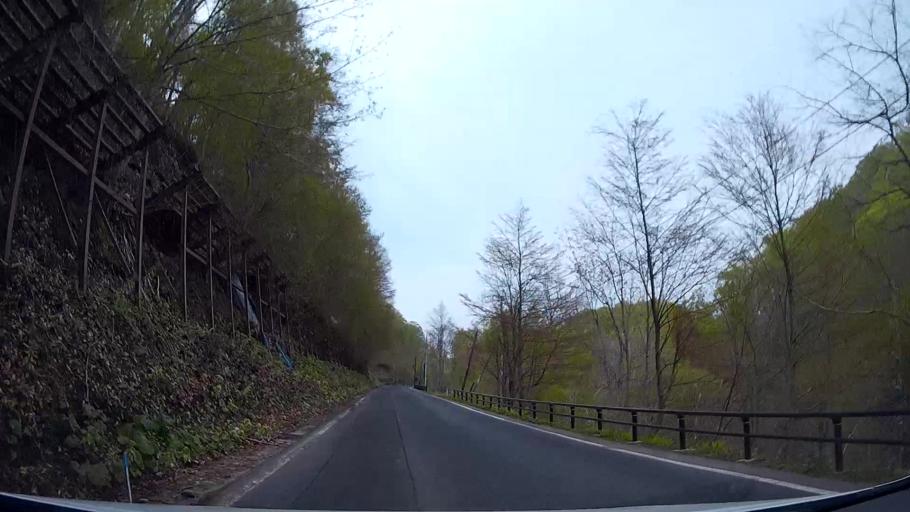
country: JP
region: Akita
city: Hanawa
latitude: 40.3904
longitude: 140.8806
